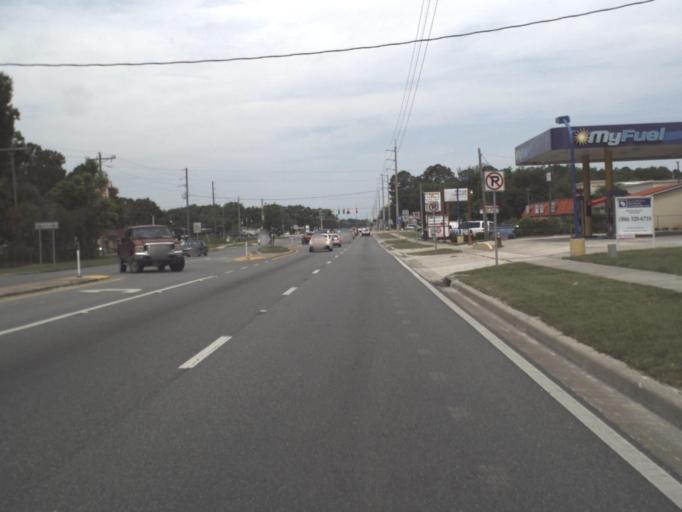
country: US
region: Florida
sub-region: Putnam County
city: Palatka
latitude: 29.6415
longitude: -81.6731
